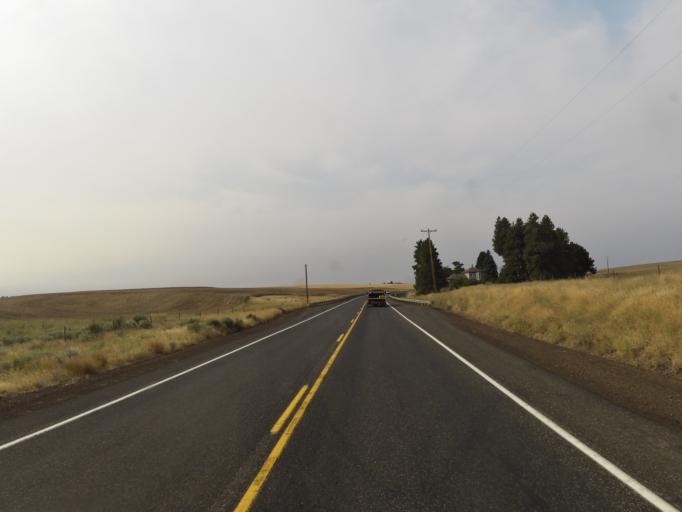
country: US
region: Oregon
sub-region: Sherman County
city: Moro
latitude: 45.4478
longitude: -120.7533
